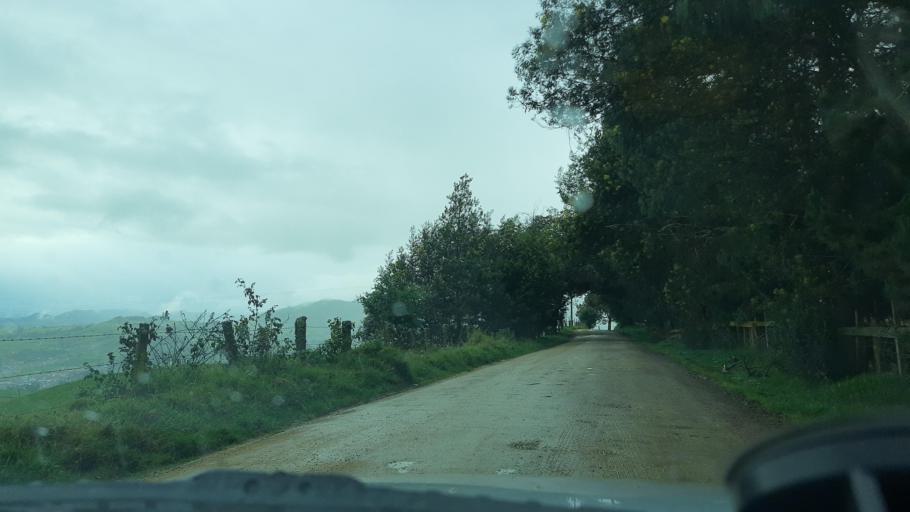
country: CO
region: Cundinamarca
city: Villapinzon
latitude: 5.2252
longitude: -73.5783
